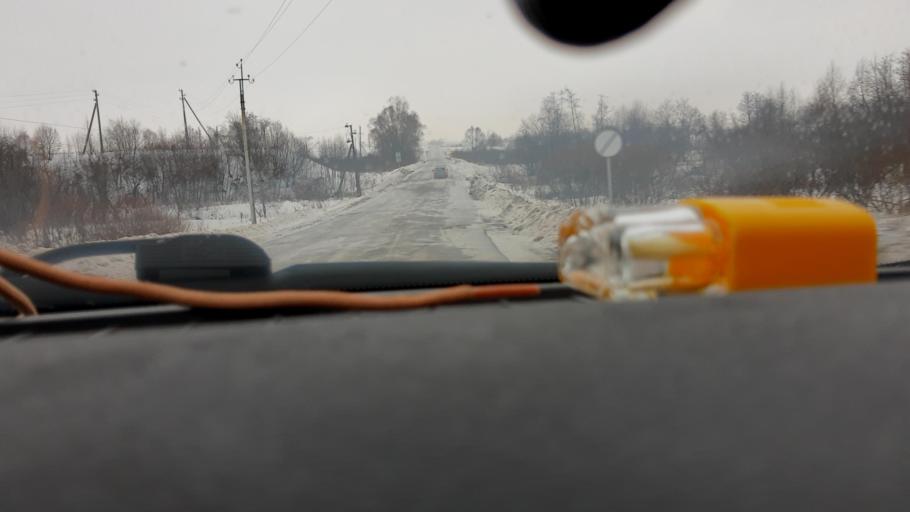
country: RU
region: Bashkortostan
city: Ulukulevo
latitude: 54.5268
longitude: 56.4282
